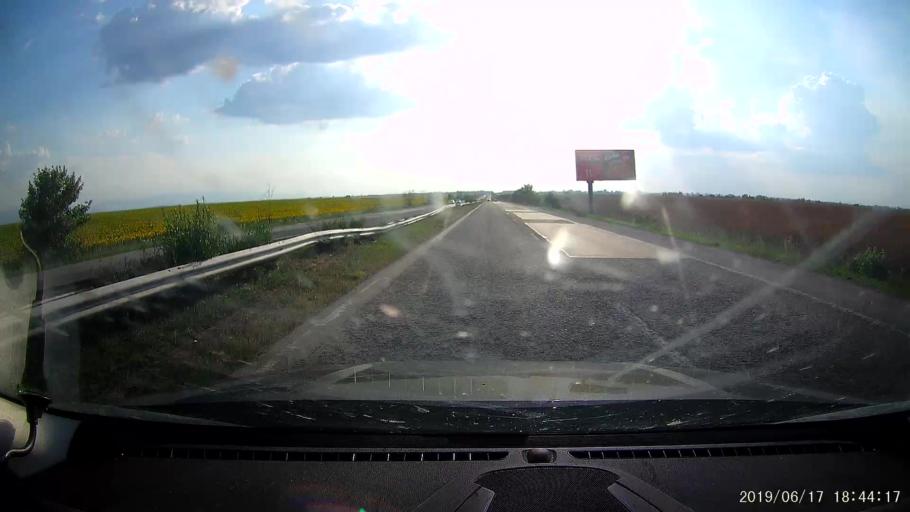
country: BG
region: Stara Zagora
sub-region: Obshtina Chirpan
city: Chirpan
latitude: 42.1927
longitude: 25.1869
